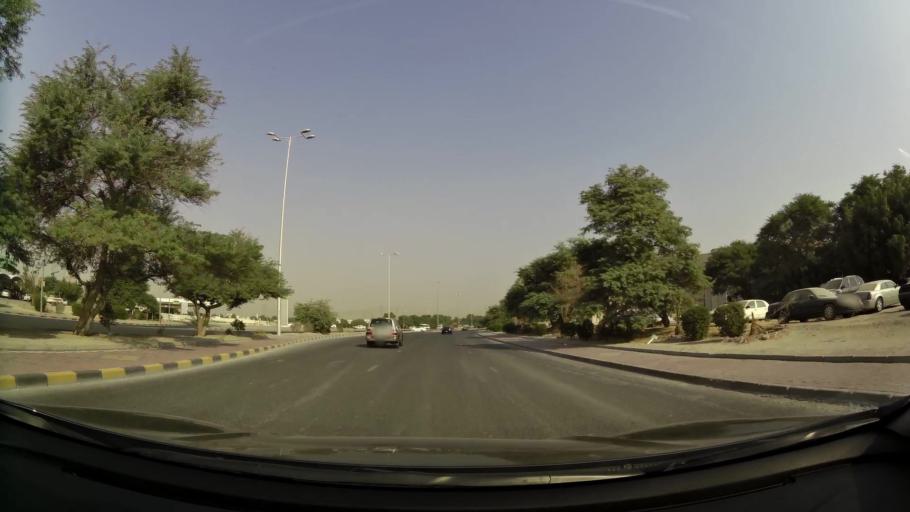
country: KW
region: Al Asimah
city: Ar Rabiyah
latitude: 29.2863
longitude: 47.8323
